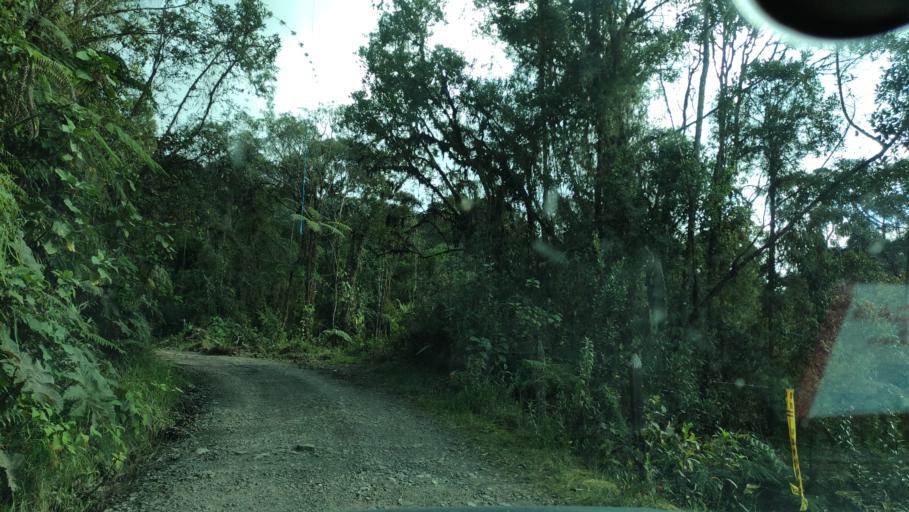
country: CO
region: Valle del Cauca
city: San Pedro
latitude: 3.8718
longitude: -76.1275
